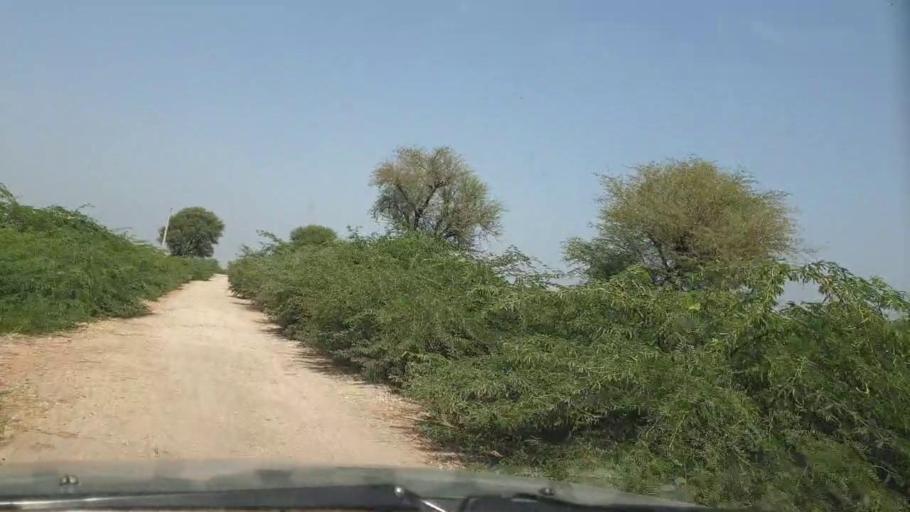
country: PK
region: Sindh
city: Tando Ghulam Ali
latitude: 25.0827
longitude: 68.8020
